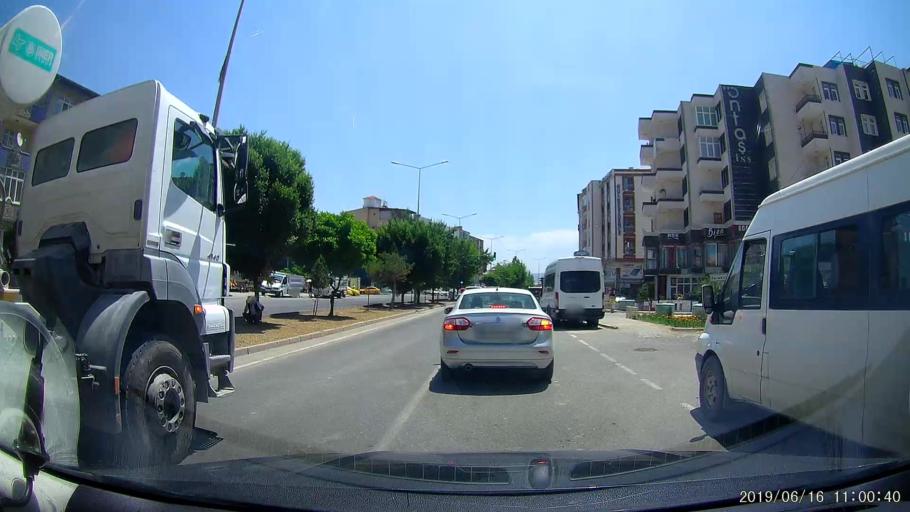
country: TR
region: Igdir
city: Igdir
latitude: 39.9180
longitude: 44.0453
